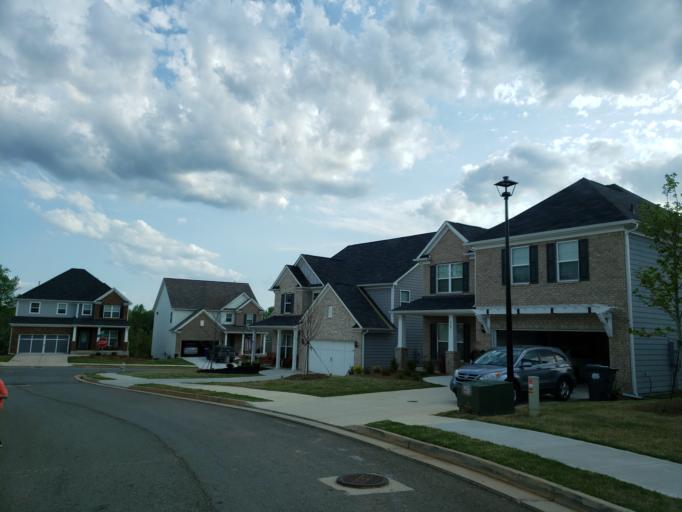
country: US
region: Georgia
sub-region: Cherokee County
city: Holly Springs
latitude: 34.1674
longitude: -84.4281
